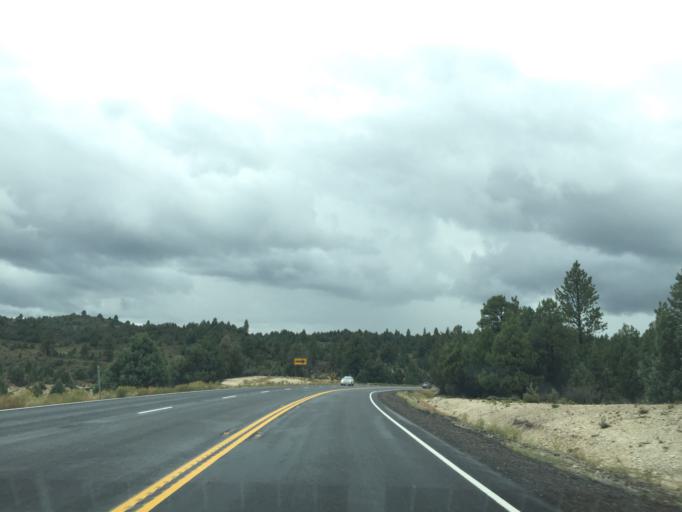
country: US
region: Utah
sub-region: Garfield County
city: Panguitch
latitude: 37.4767
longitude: -112.5133
